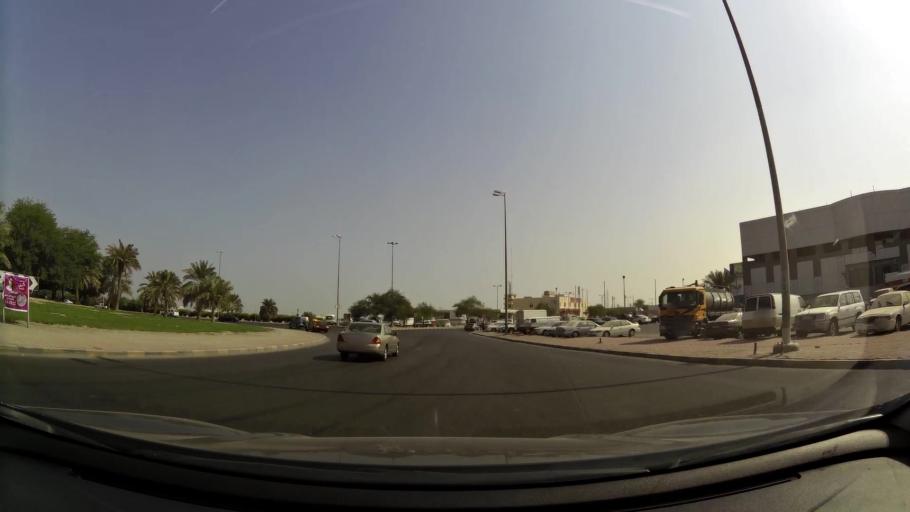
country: KW
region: Al Ahmadi
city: Al Fahahil
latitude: 29.0734
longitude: 48.1247
